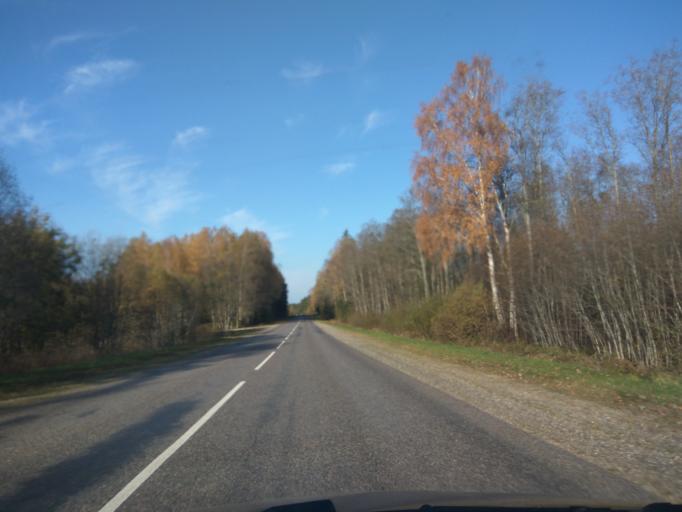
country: LV
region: Kuldigas Rajons
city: Kuldiga
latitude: 57.0579
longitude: 21.8157
